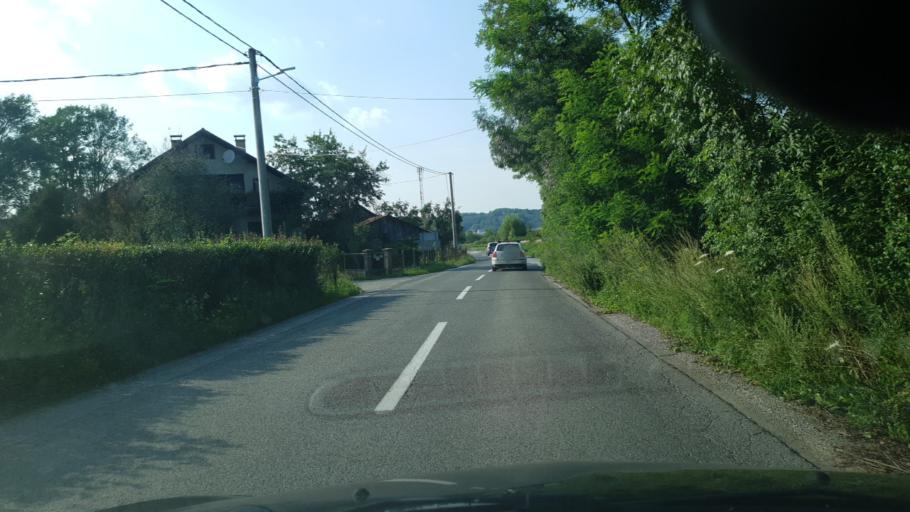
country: HR
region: Krapinsko-Zagorska
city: Oroslavje
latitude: 46.0006
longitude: 15.8840
